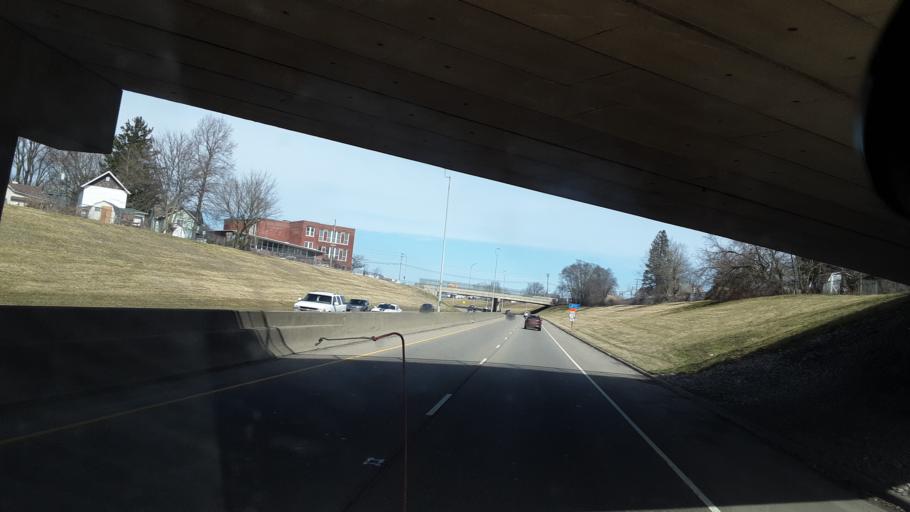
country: US
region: Ohio
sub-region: Licking County
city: Newark
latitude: 40.0452
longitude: -82.4247
